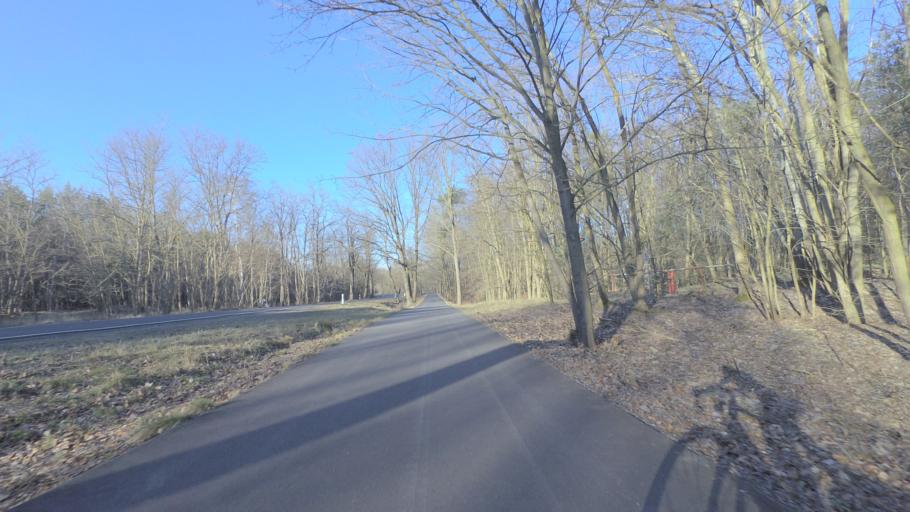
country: DE
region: Brandenburg
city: Sperenberg
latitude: 52.0210
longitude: 13.3189
